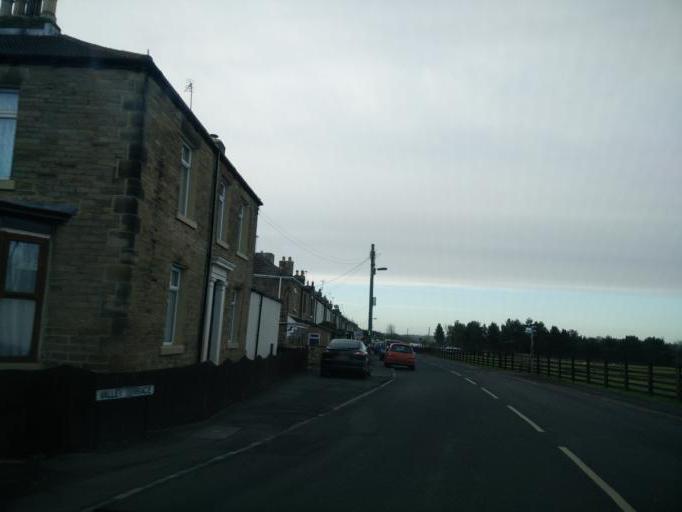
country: GB
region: England
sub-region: County Durham
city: Crook
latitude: 54.6932
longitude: -1.7438
